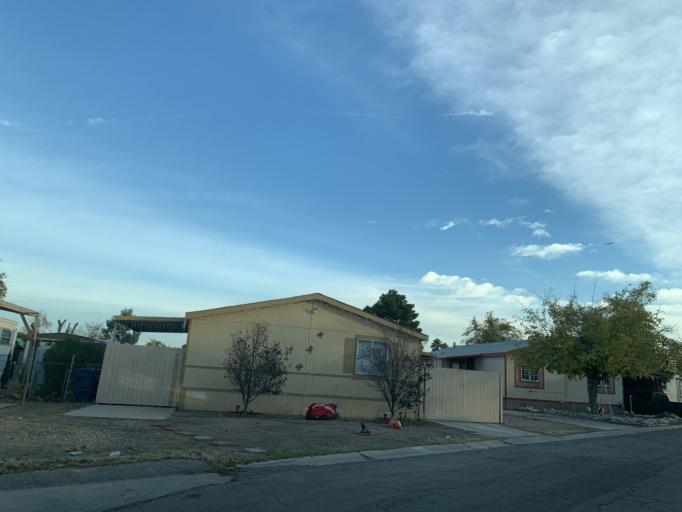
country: US
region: Nevada
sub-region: Clark County
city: Spring Valley
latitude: 36.1036
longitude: -115.2218
